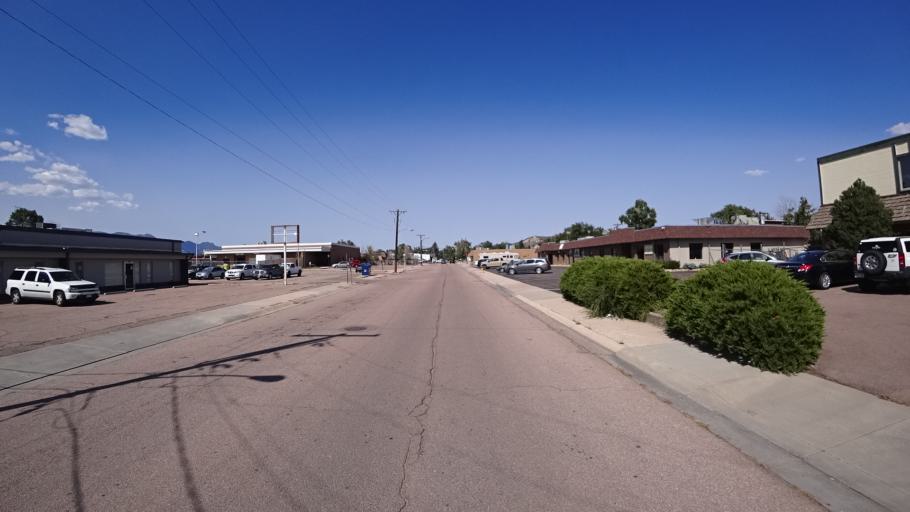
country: US
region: Colorado
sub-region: El Paso County
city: Colorado Springs
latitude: 38.8727
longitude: -104.8112
